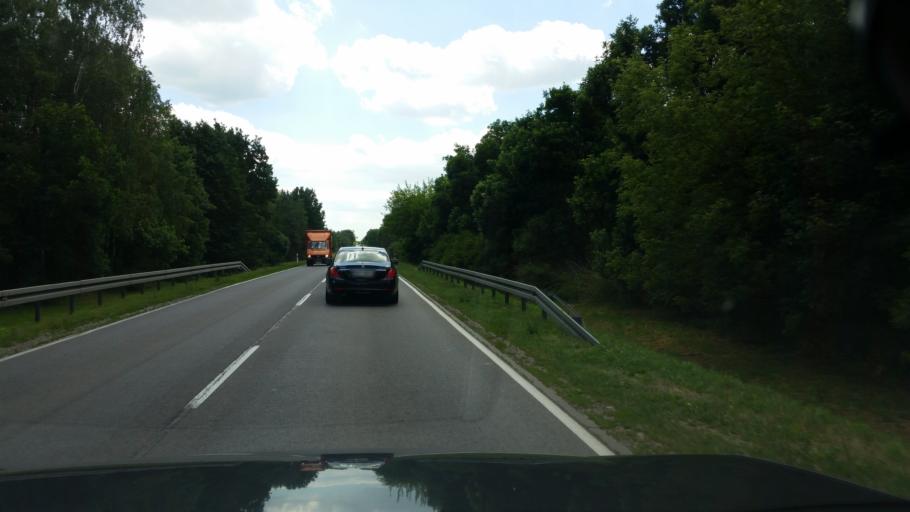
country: PL
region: Masovian Voivodeship
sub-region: Powiat ostrowski
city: Ostrow Mazowiecka
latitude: 52.8515
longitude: 21.8680
